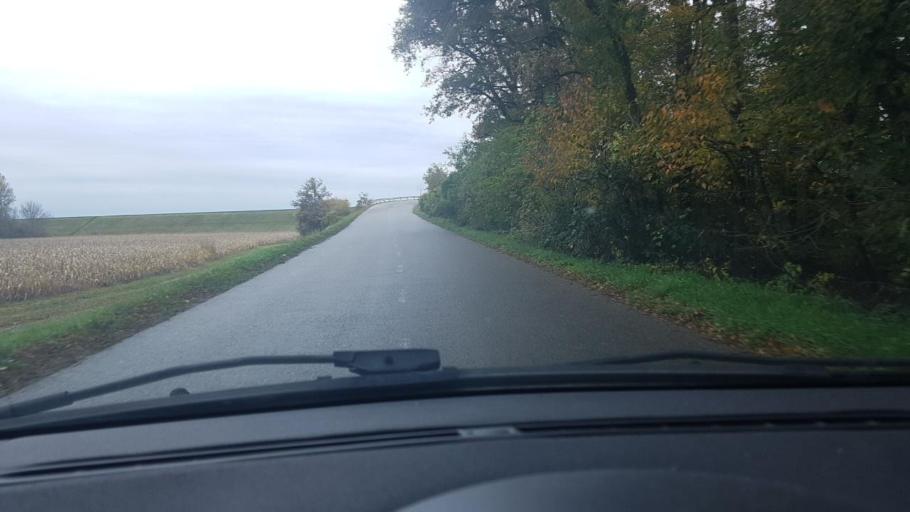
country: SI
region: Starse
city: Starse
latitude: 46.4539
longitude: 15.7630
